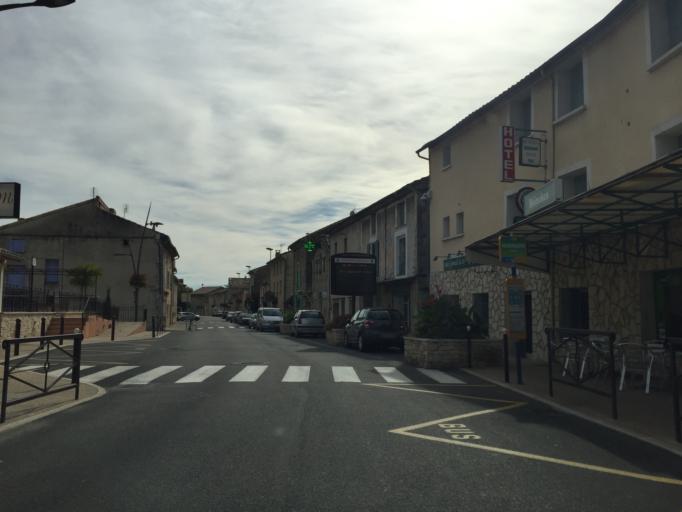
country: FR
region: Provence-Alpes-Cote d'Azur
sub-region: Departement du Vaucluse
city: Mondragon
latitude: 44.2388
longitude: 4.7127
